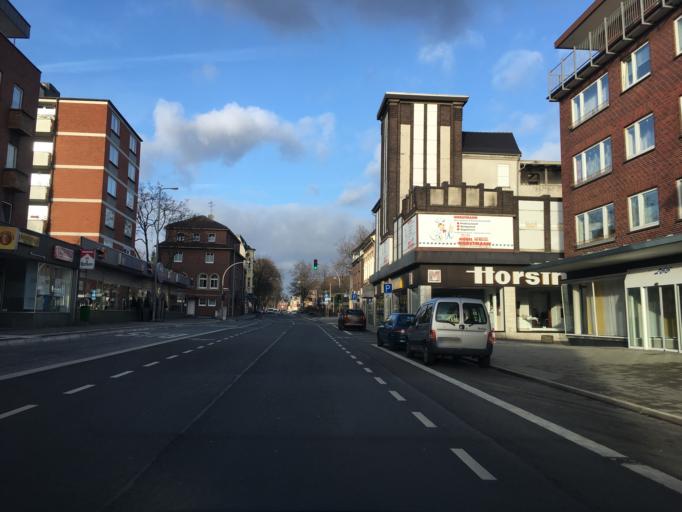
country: DE
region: North Rhine-Westphalia
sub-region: Regierungsbezirk Dusseldorf
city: Oberhausen
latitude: 51.5185
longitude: 6.8466
